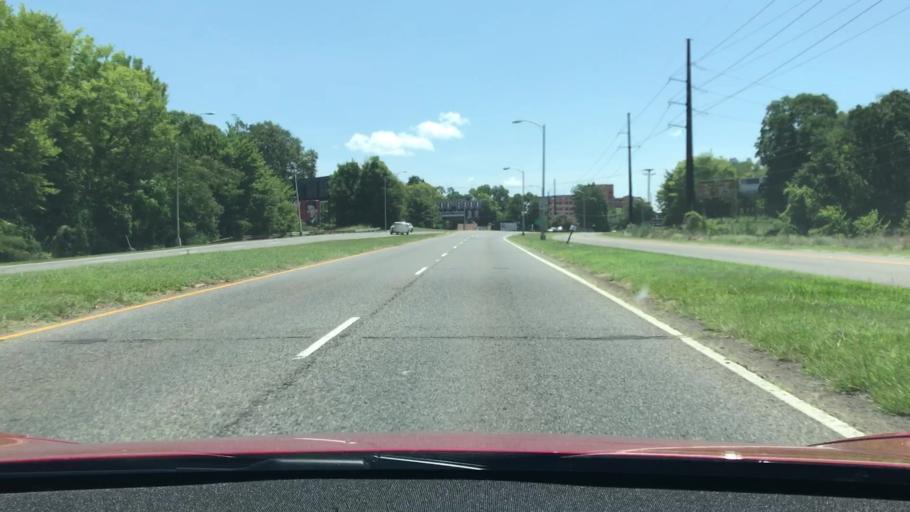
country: US
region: Louisiana
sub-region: Bossier Parish
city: Bossier City
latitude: 32.5039
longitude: -93.7291
